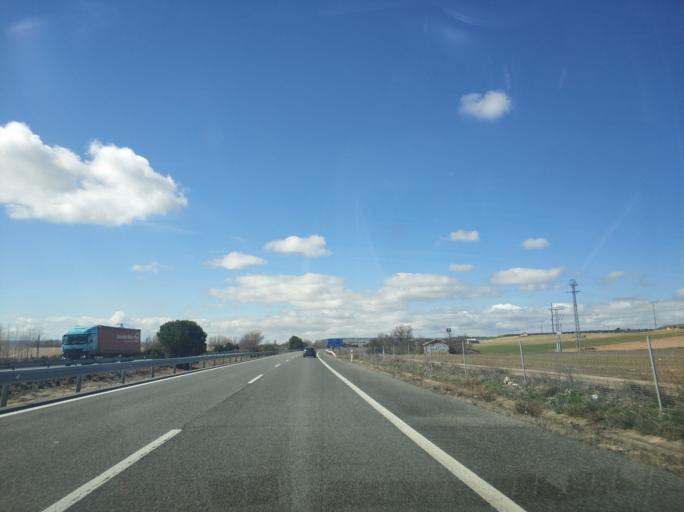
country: ES
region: Castille and Leon
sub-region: Provincia de Burgos
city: Villaverde-Mogina
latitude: 42.1800
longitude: -4.0500
